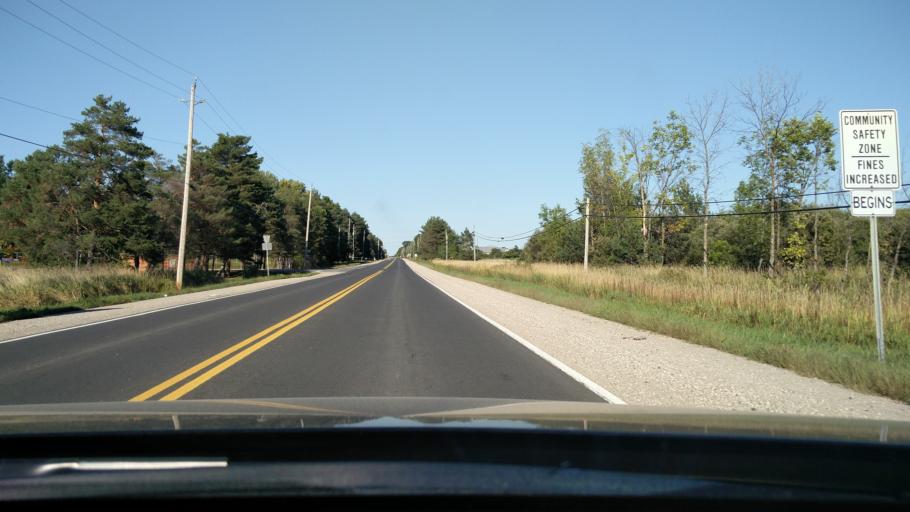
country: CA
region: Ontario
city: Perth
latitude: 44.8842
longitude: -76.2532
